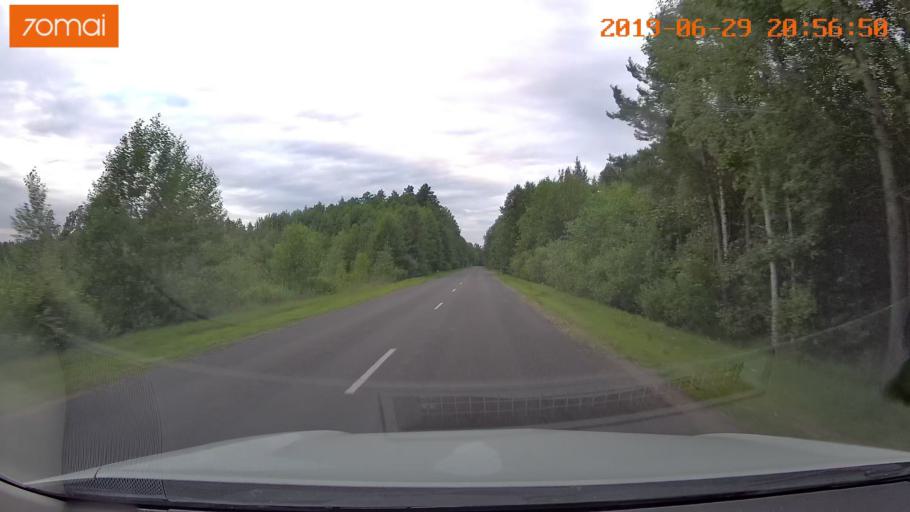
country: BY
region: Brest
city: Hantsavichy
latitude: 52.7107
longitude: 26.3688
